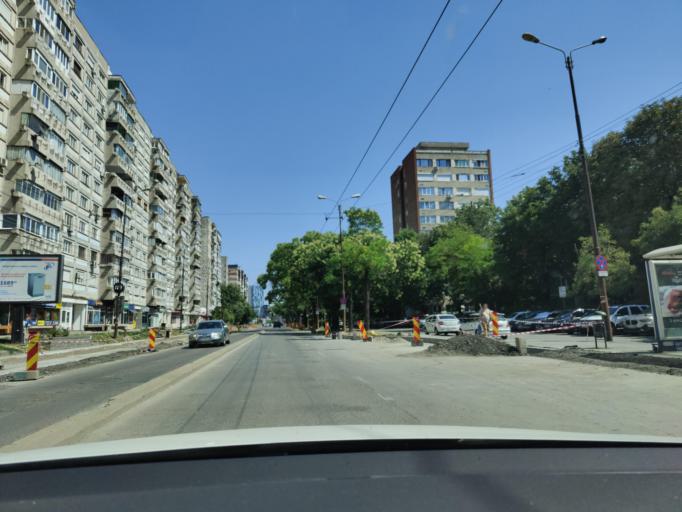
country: RO
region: Timis
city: Timisoara
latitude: 45.7618
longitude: 21.2137
